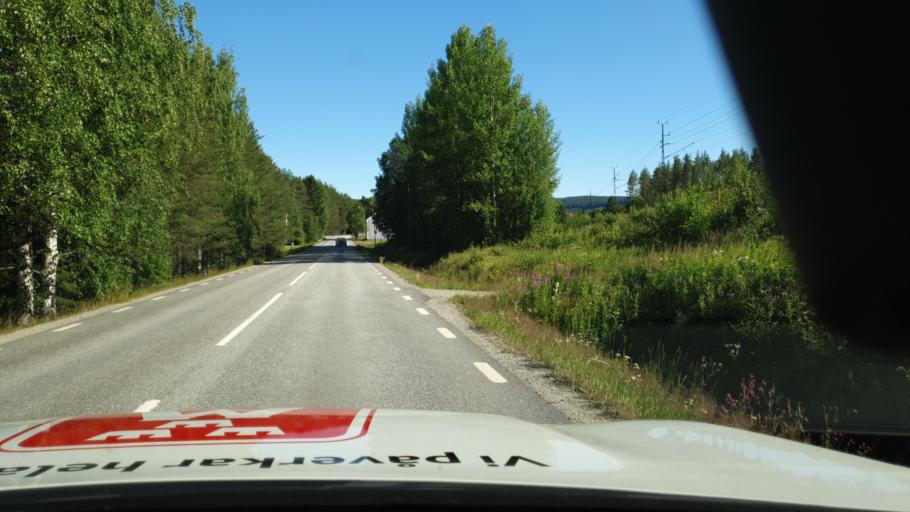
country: SE
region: Vaesterbotten
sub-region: Vindelns Kommun
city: Vindeln
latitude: 64.2228
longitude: 19.7071
